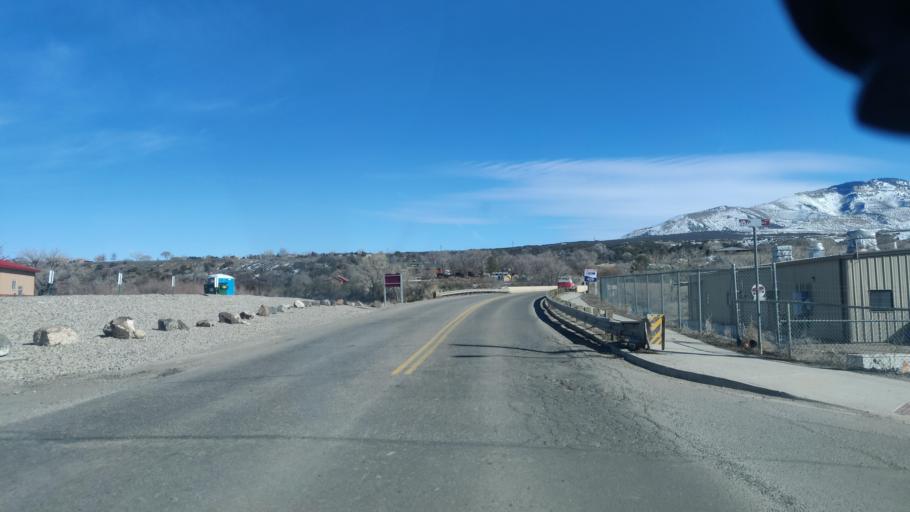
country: US
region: Colorado
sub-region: Garfield County
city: Parachute
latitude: 39.4535
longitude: -108.0426
